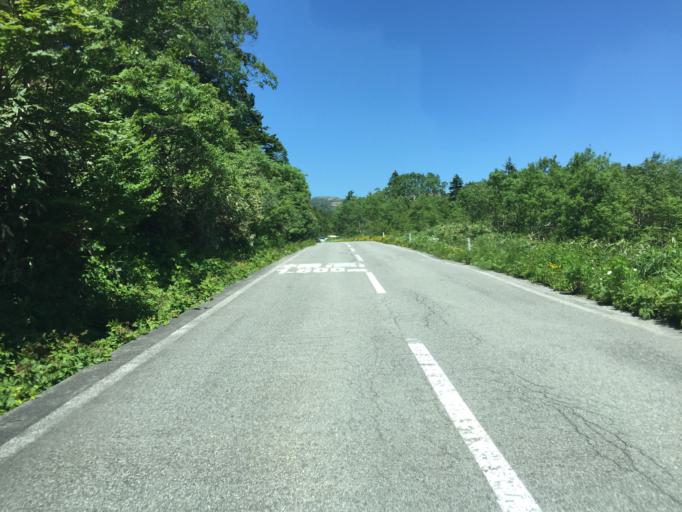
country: JP
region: Fukushima
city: Inawashiro
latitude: 37.7024
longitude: 140.2476
